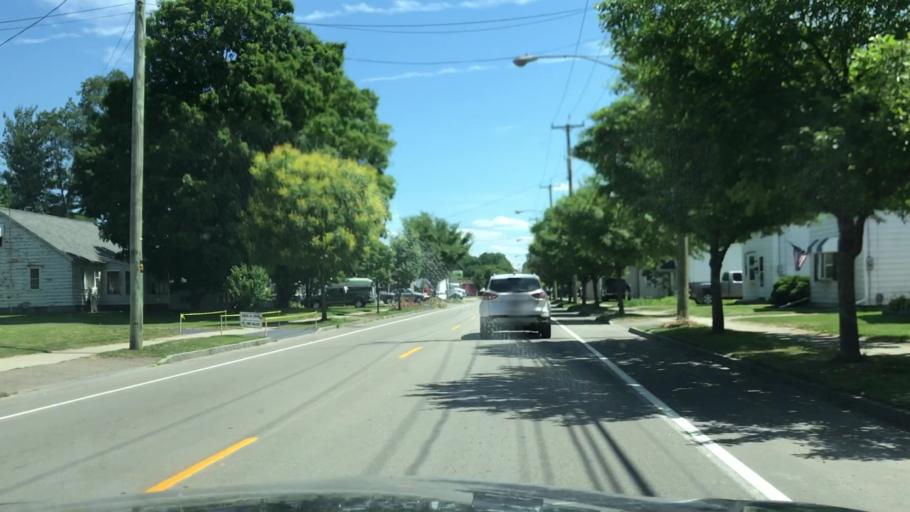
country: US
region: New York
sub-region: Livingston County
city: Mount Morris
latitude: 42.7329
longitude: -77.8784
